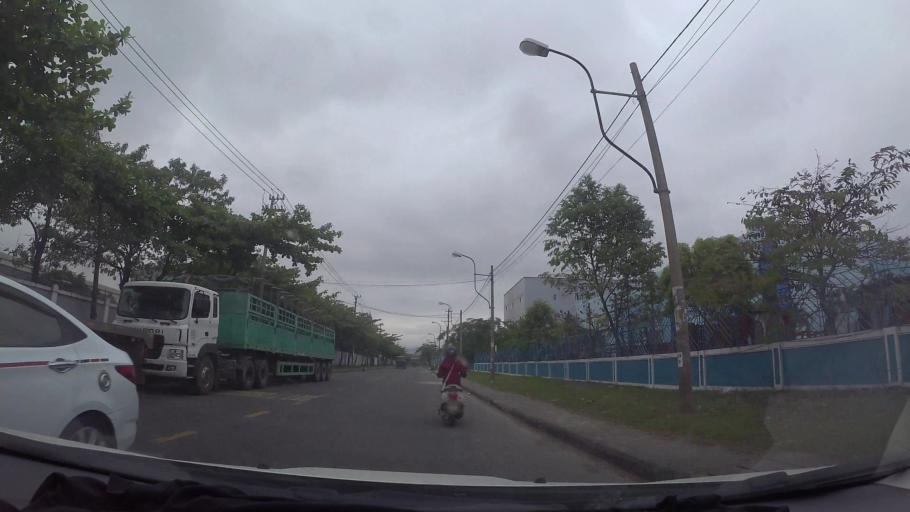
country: VN
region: Da Nang
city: Lien Chieu
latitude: 16.0811
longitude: 108.1425
